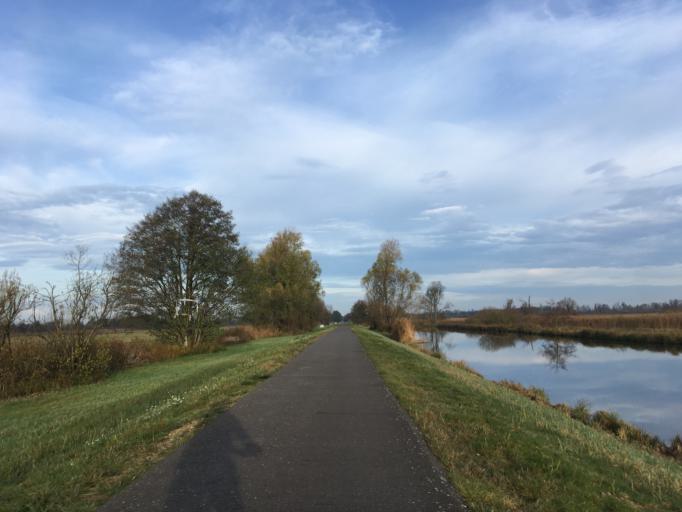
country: DE
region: Brandenburg
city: Luebben
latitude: 51.9067
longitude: 13.9259
